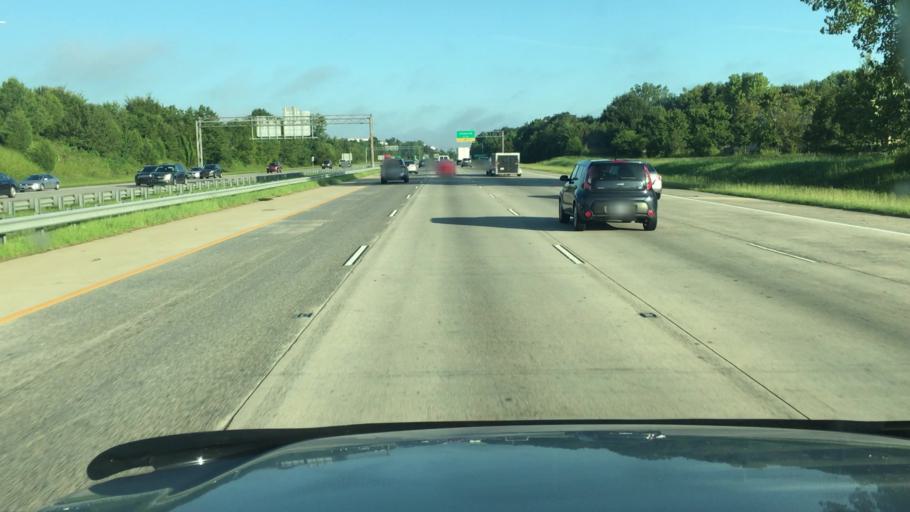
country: US
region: North Carolina
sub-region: Mecklenburg County
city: Pineville
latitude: 35.1444
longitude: -80.9358
